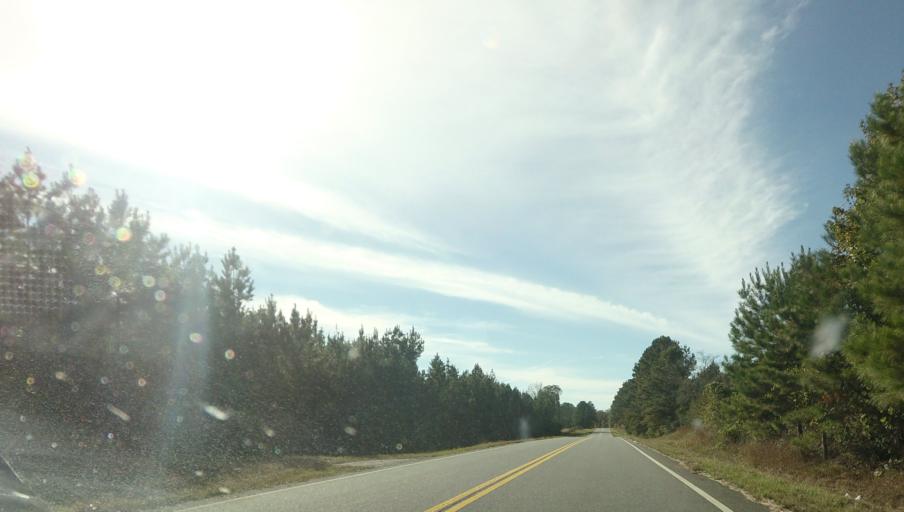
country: US
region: Georgia
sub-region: Talbot County
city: Talbotton
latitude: 32.7124
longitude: -84.3650
